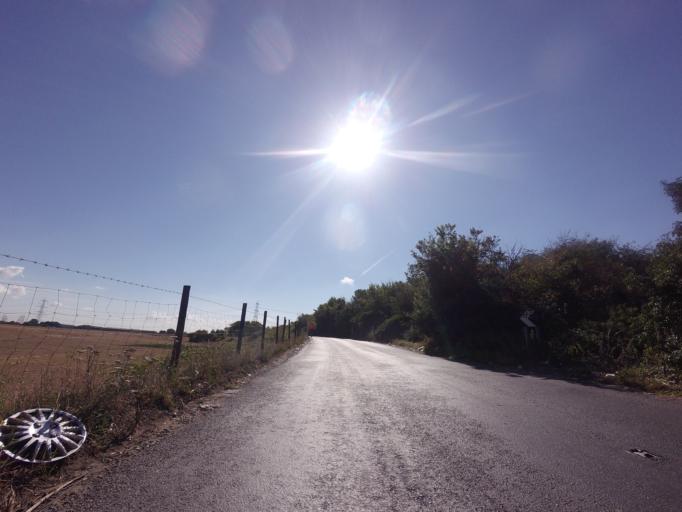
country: GB
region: England
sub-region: Kent
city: Gravesend
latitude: 51.4318
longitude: 0.4241
